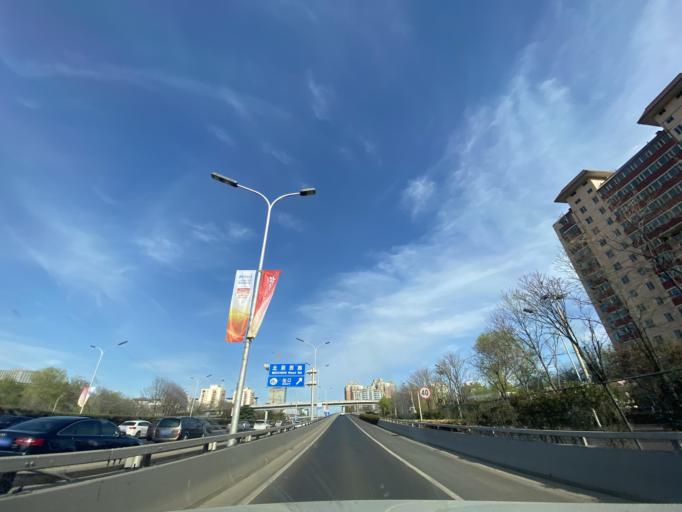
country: CN
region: Beijing
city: Datun
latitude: 39.9859
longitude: 116.3678
